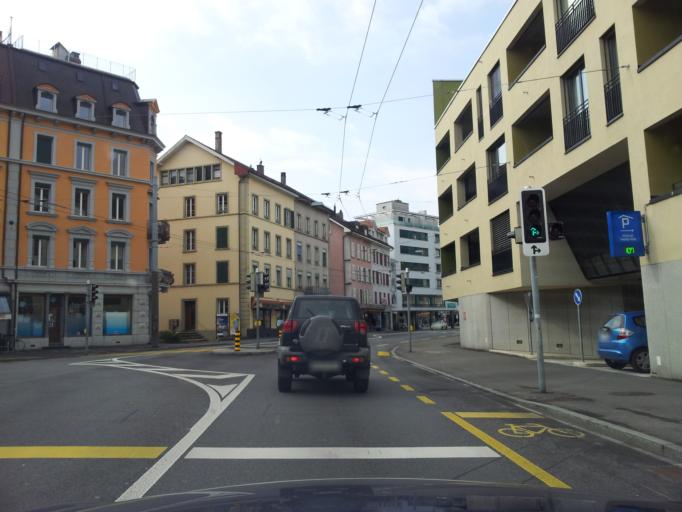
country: CH
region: Bern
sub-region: Biel/Bienne District
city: Biel/Bienne
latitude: 47.1423
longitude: 7.2488
